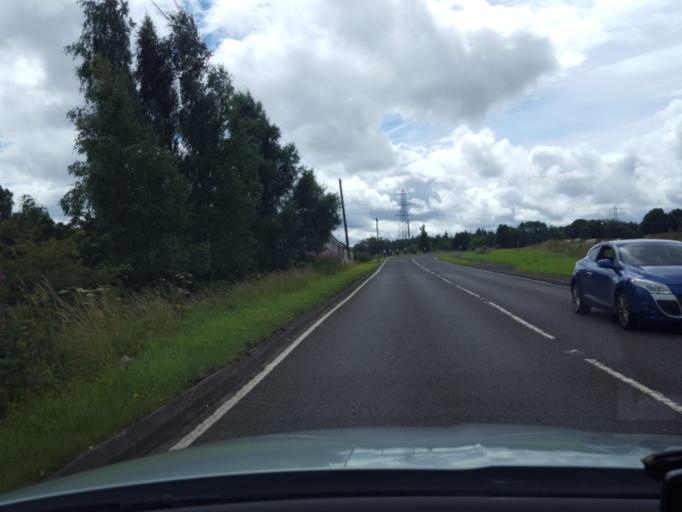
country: GB
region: Scotland
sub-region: Stirling
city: Cowie
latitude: 56.0488
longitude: -3.8572
